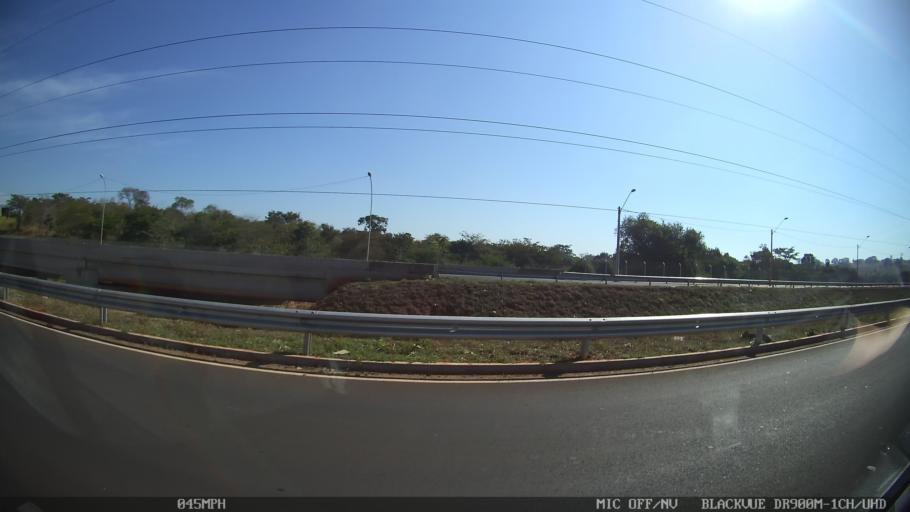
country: BR
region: Sao Paulo
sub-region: Sao Jose Do Rio Preto
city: Sao Jose do Rio Preto
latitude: -20.7621
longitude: -49.3742
